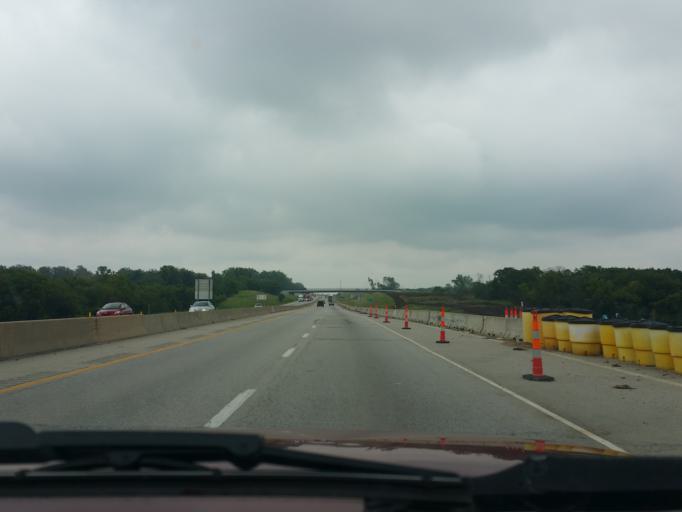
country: US
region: Kansas
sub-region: Wyandotte County
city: Bonner Springs
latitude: 39.0986
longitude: -94.8721
